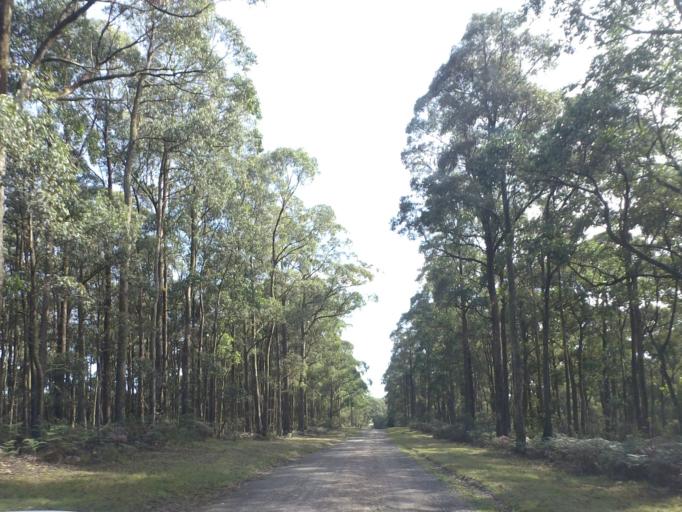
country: AU
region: Victoria
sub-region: Moorabool
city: Bacchus Marsh
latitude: -37.4661
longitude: 144.2157
